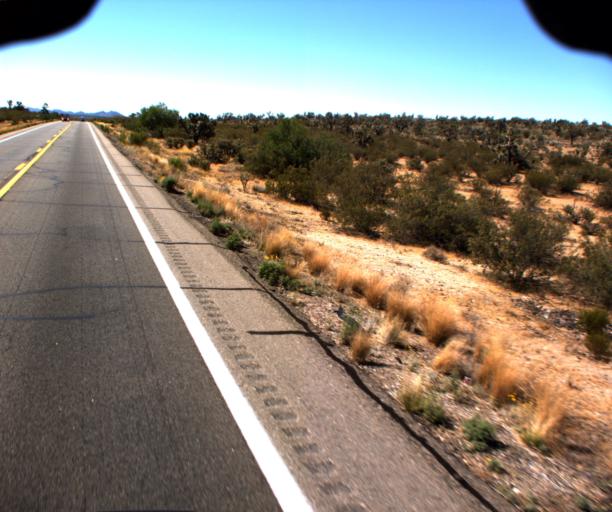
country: US
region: Arizona
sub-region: Yavapai County
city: Congress
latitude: 34.2405
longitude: -113.0761
